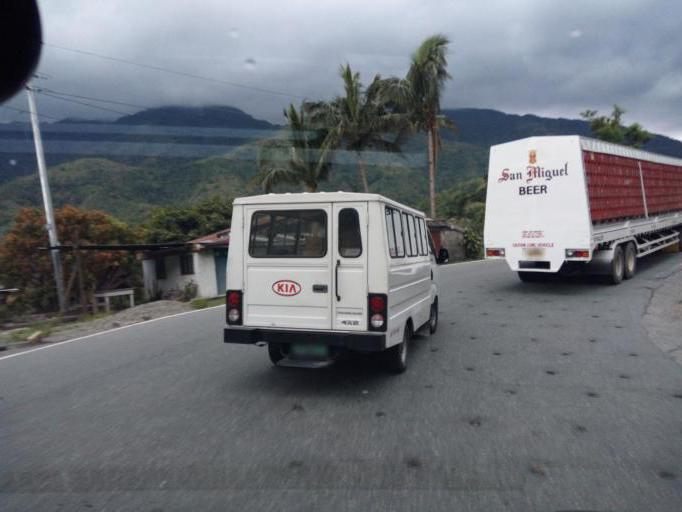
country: PH
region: Cagayan Valley
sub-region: Province of Nueva Vizcaya
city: Santa Fe
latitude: 16.1087
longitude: 120.9269
